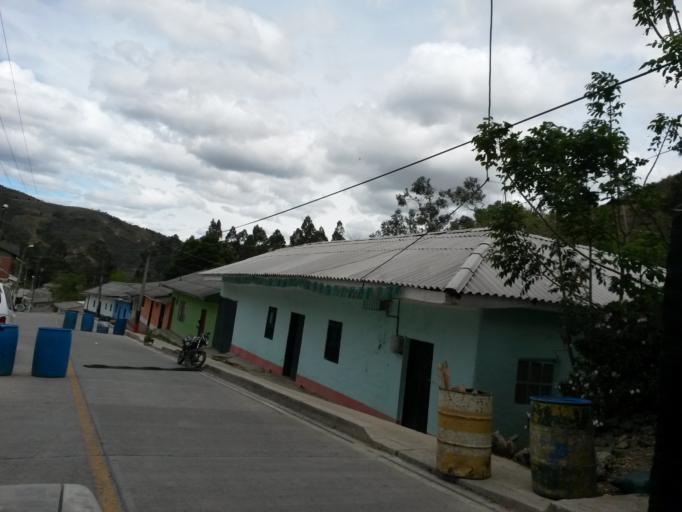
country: CO
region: Cauca
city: Totoro
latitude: 2.5114
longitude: -76.4034
